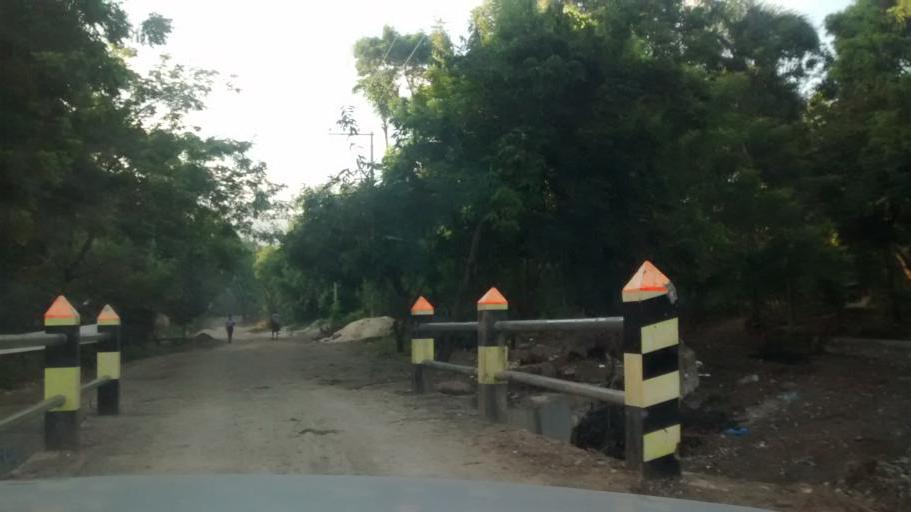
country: HT
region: Ouest
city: Grangwav
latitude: 18.4225
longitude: -72.7832
